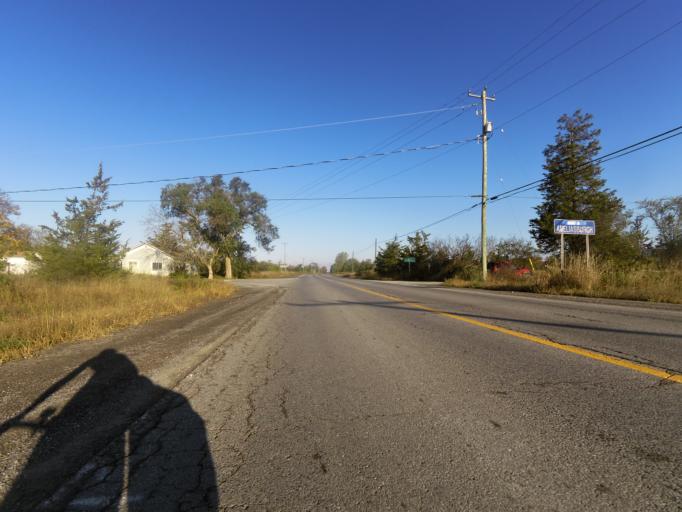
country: CA
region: Ontario
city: Belleville
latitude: 44.0457
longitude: -77.3831
